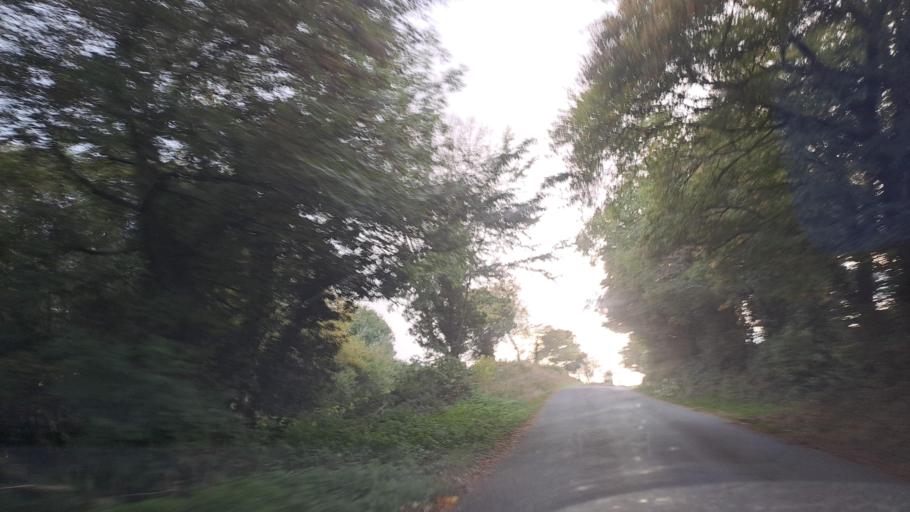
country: IE
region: Ulster
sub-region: County Monaghan
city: Castleblayney
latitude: 54.0437
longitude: -6.8409
